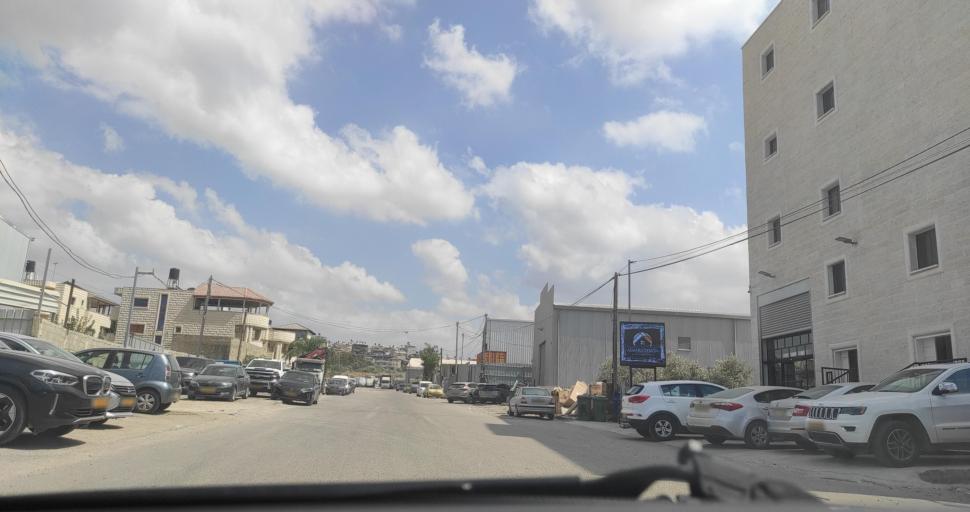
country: IL
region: Central District
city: Kafr Qasim
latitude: 32.1164
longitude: 34.9584
